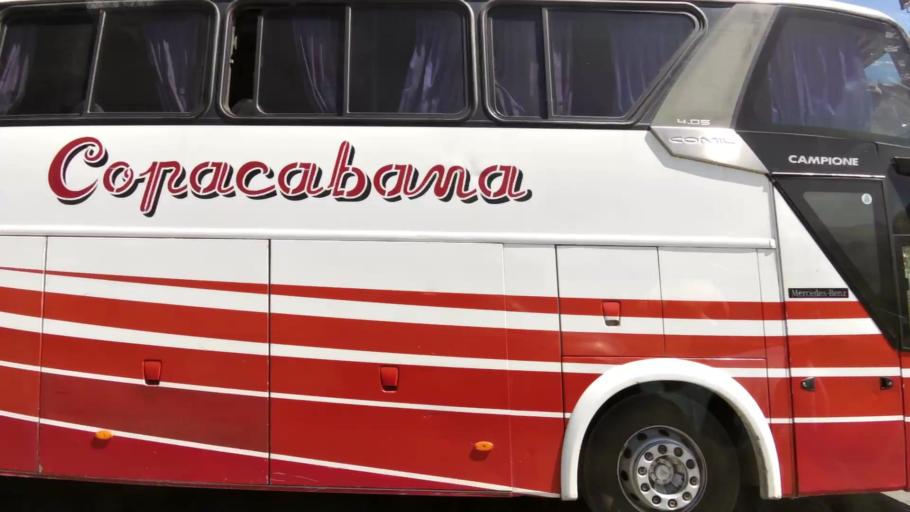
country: BO
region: La Paz
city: La Paz
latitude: -16.4992
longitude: -68.1630
